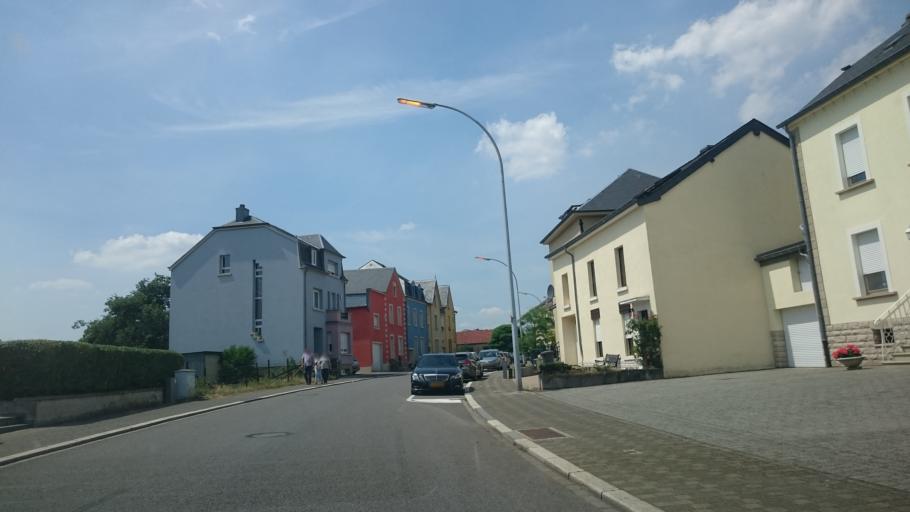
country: LU
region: Luxembourg
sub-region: Canton de Capellen
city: Mamer
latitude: 49.6275
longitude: 6.0281
